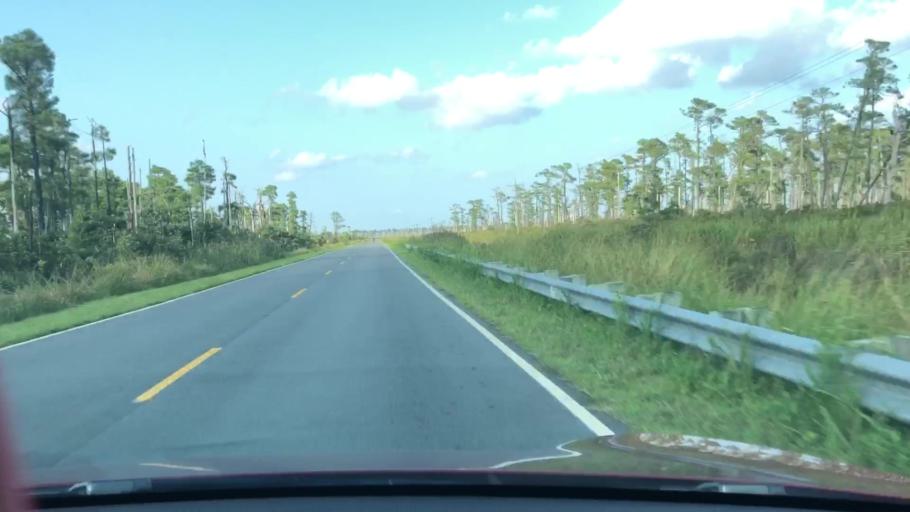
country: US
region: North Carolina
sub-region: Dare County
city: Wanchese
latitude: 35.6151
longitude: -75.7936
